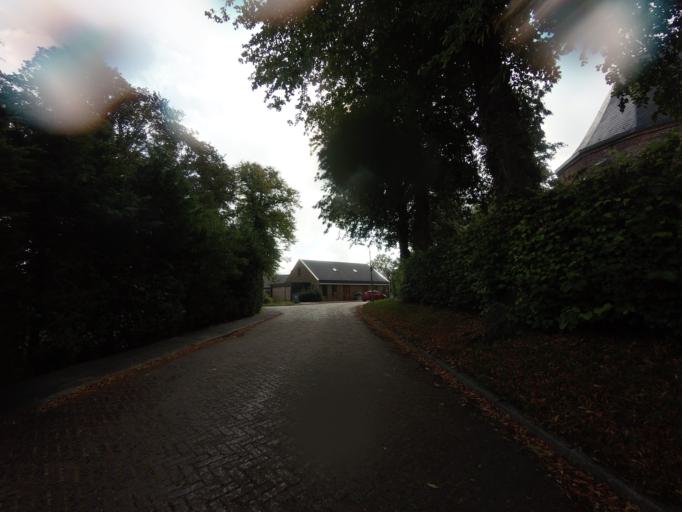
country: NL
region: Friesland
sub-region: Gemeente Leeuwarden
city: Wirdum
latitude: 53.1503
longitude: 5.8045
